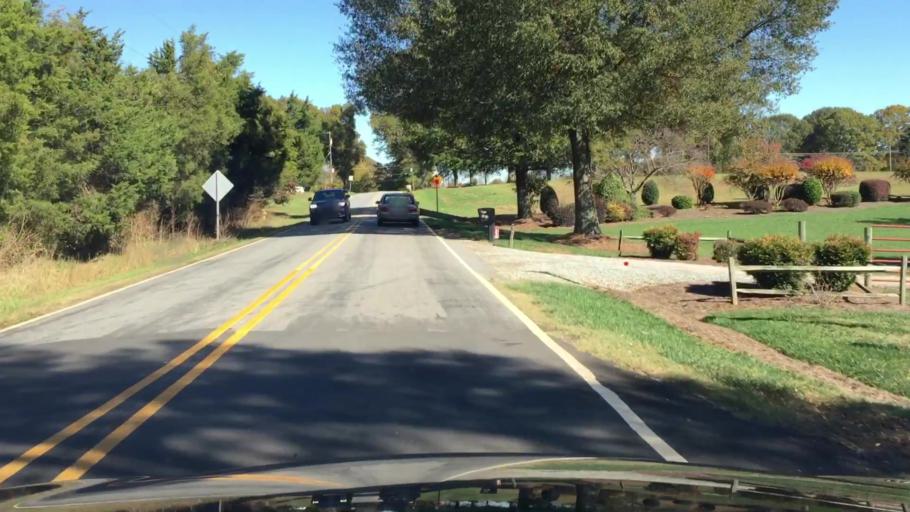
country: US
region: North Carolina
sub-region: Iredell County
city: Mooresville
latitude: 35.5466
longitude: -80.7742
